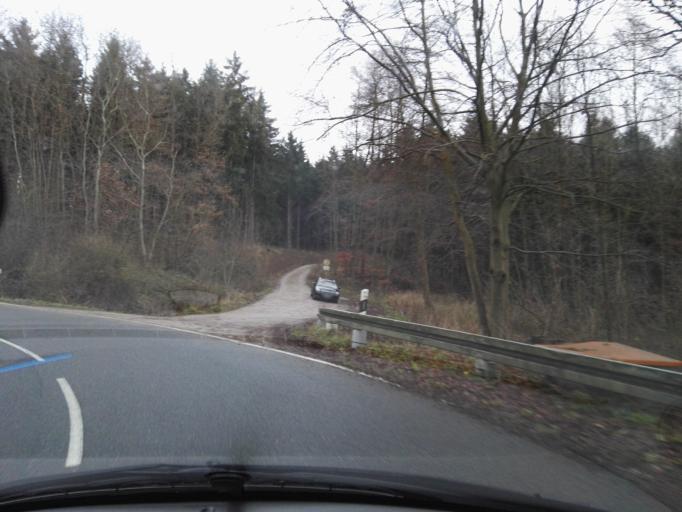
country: DE
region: Lower Saxony
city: Diekholzen
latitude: 52.0744
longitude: 9.9087
